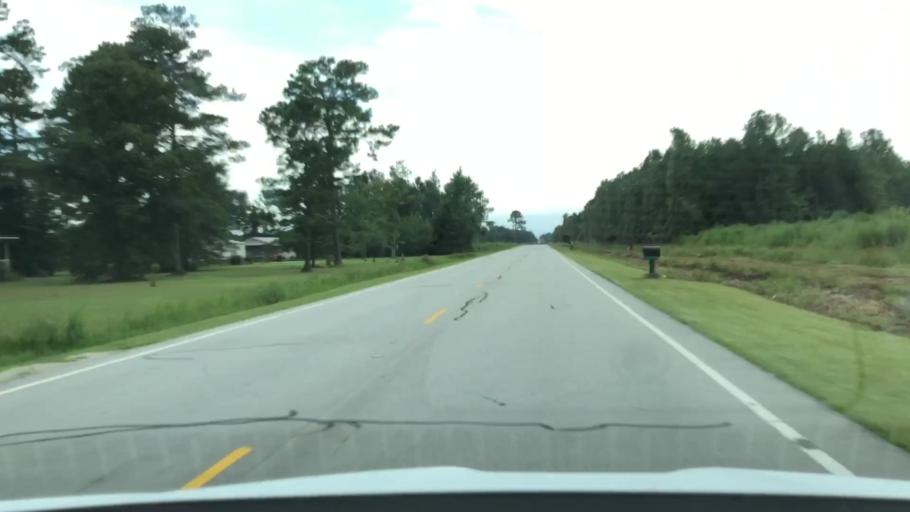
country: US
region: North Carolina
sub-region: Lenoir County
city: Kinston
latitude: 35.1241
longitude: -77.5194
